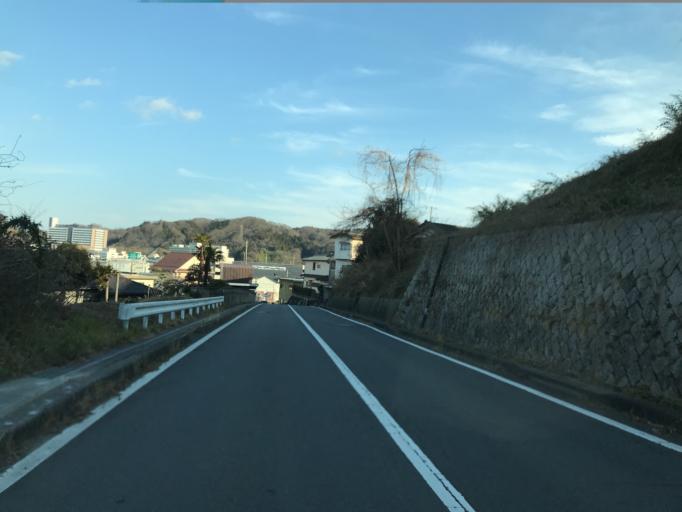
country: JP
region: Fukushima
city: Iwaki
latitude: 37.0436
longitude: 140.8580
